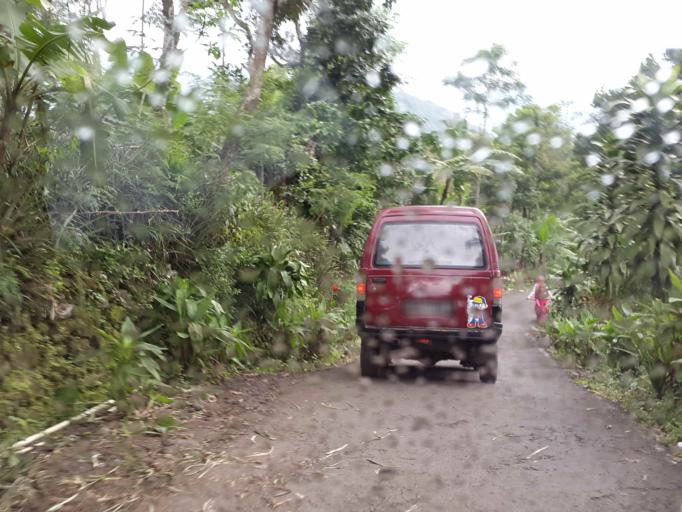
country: ID
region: Central Java
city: Randudongkal
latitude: -7.1766
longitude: 109.3208
